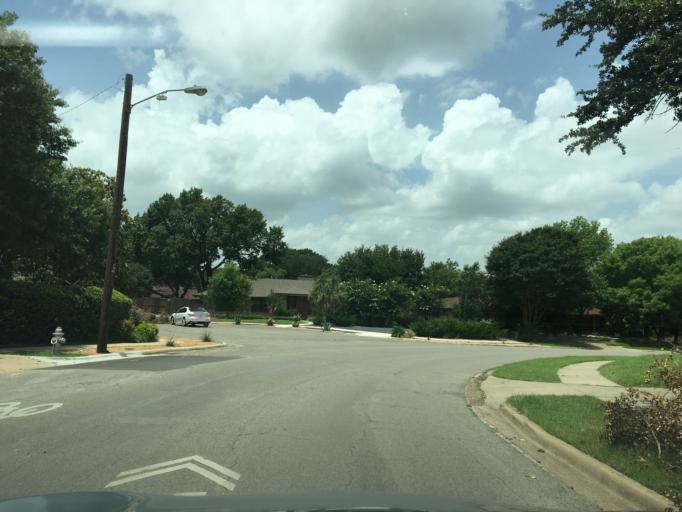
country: US
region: Texas
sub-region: Dallas County
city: University Park
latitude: 32.9009
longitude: -96.7866
